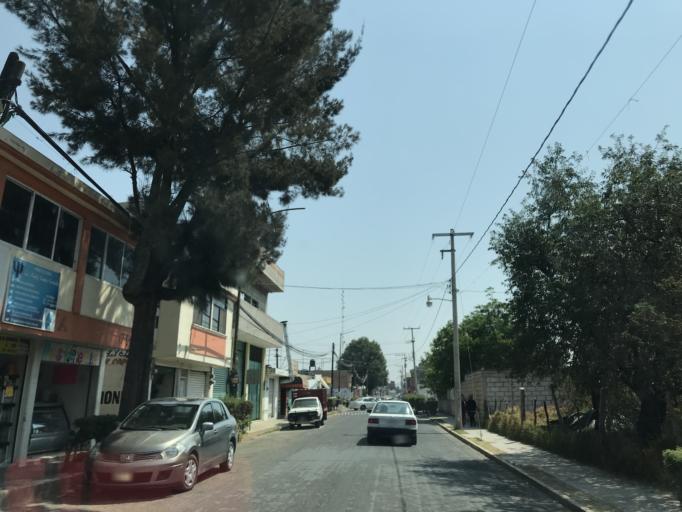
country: MX
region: Tlaxcala
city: Yauhquemehcan
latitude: 19.4039
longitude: -98.1851
